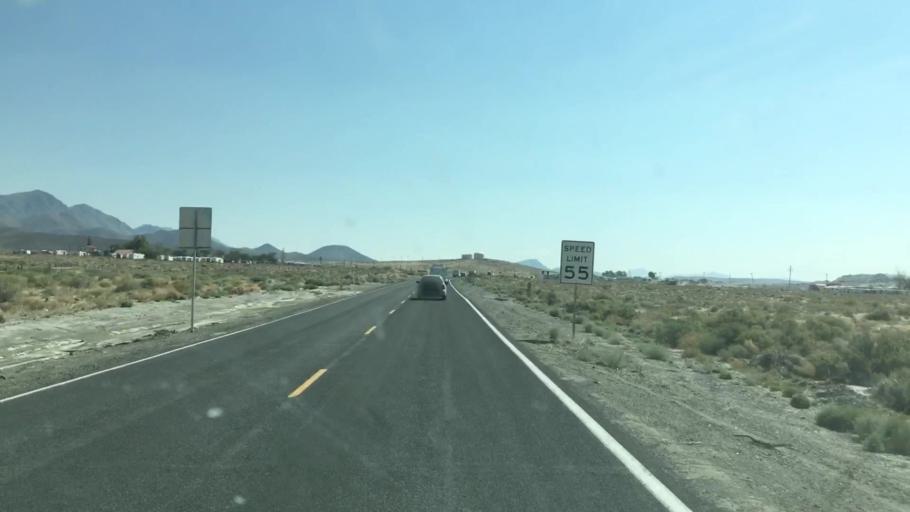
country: US
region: Nevada
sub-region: Pershing County
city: Lovelock
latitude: 40.5818
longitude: -119.3351
